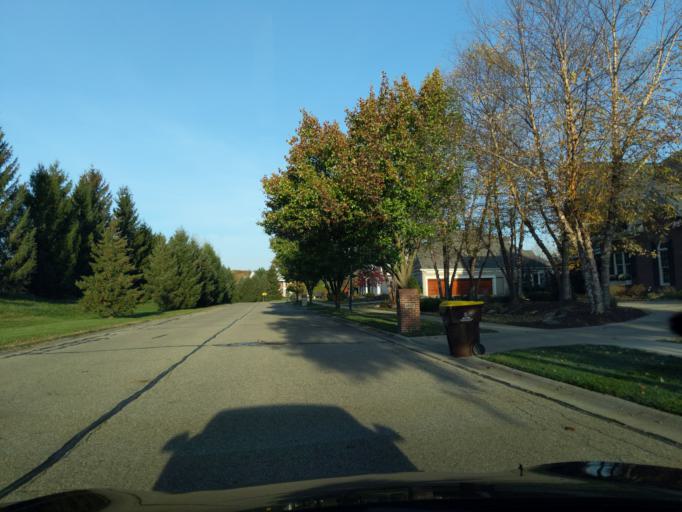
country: US
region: Michigan
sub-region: Clinton County
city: Bath
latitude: 42.7992
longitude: -84.4697
